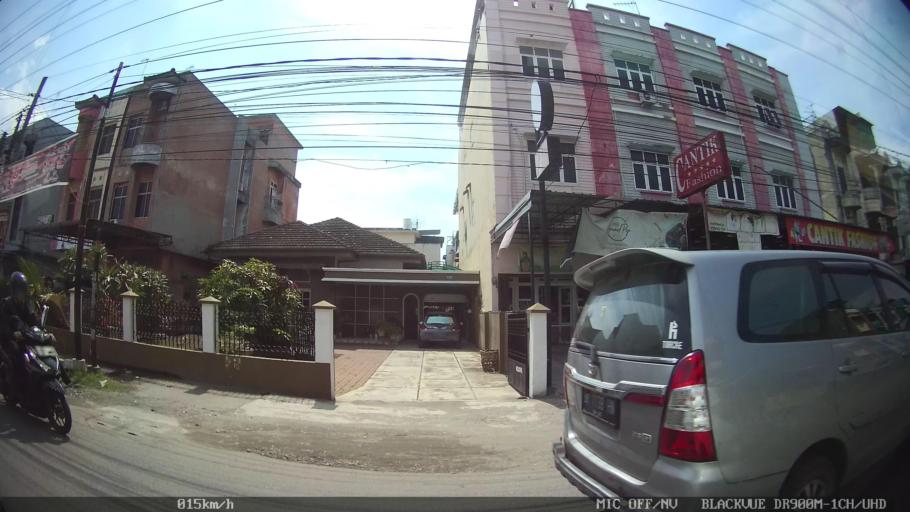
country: ID
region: North Sumatra
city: Medan
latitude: 3.6123
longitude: 98.6654
